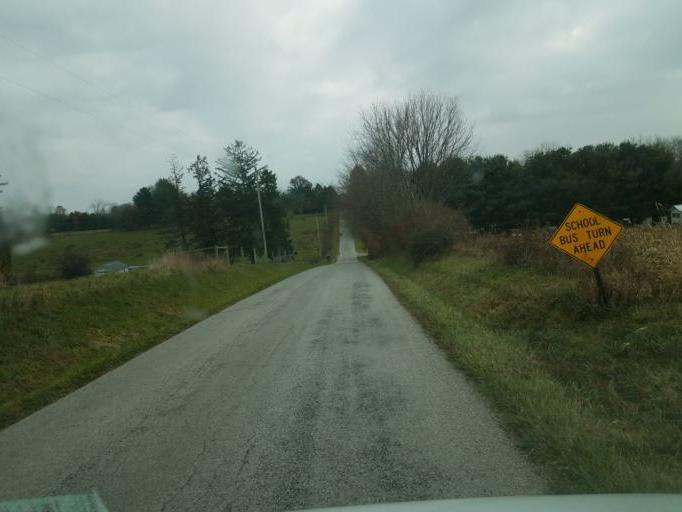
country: US
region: Ohio
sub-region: Knox County
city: Fredericktown
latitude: 40.5430
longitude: -82.5128
